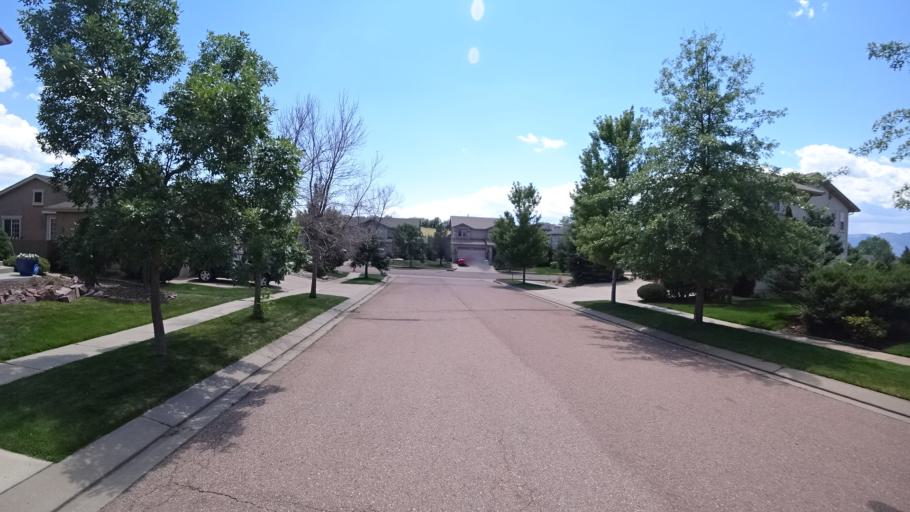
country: US
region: Colorado
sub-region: El Paso County
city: Black Forest
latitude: 38.9686
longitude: -104.7689
